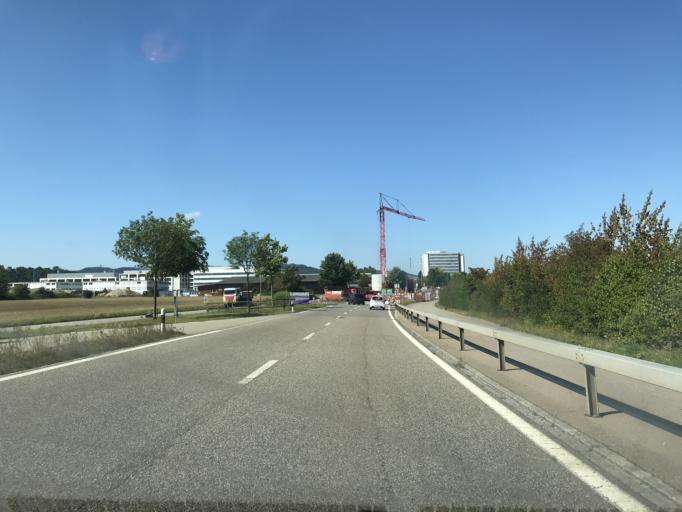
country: CH
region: Aargau
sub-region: Bezirk Rheinfelden
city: Kaiseraugst
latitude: 47.5421
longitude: 7.7486
